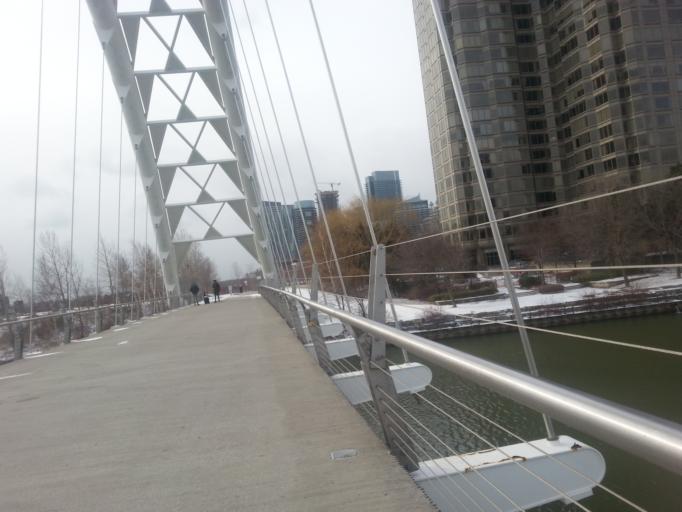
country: CA
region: Ontario
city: Toronto
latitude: 43.6320
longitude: -79.4713
